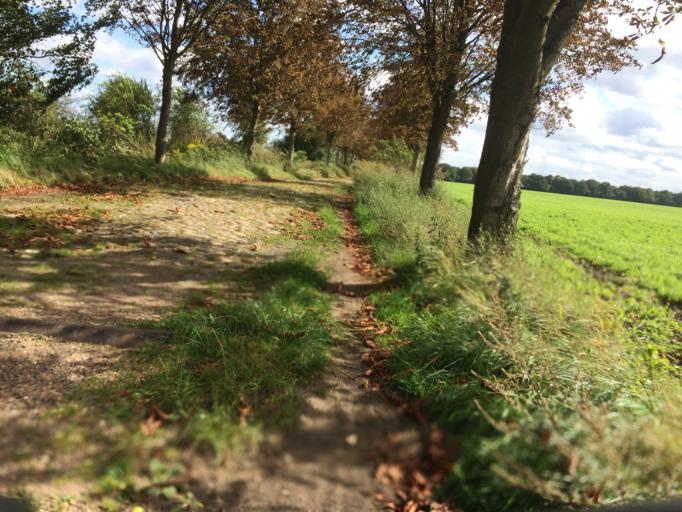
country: DE
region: Berlin
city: Blankenburg
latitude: 52.5838
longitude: 13.4515
